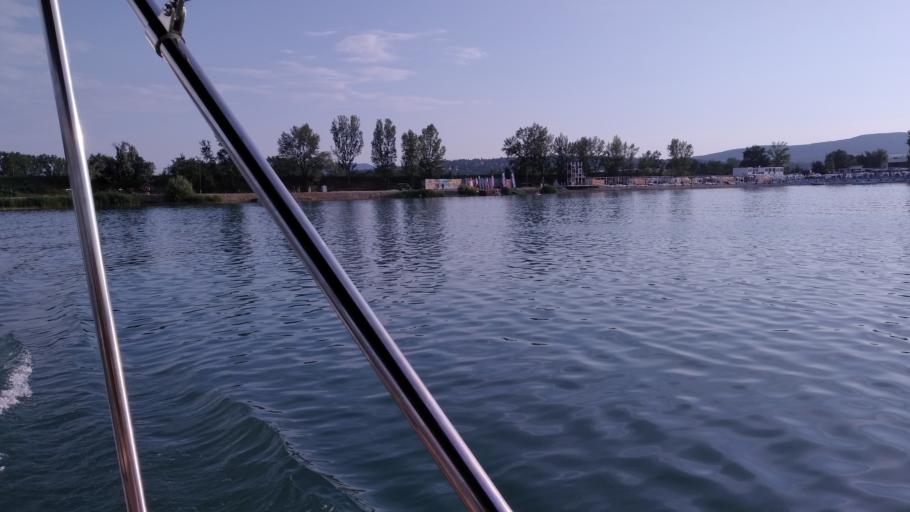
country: HU
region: Pest
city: Budakalasz
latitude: 47.6239
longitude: 19.0755
